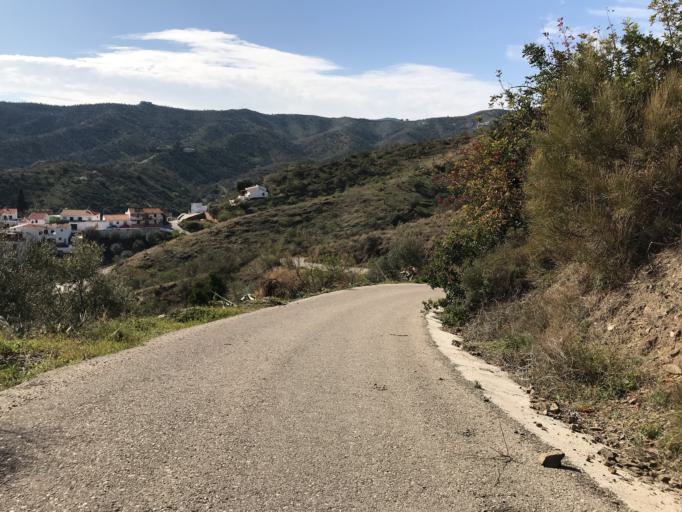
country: ES
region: Andalusia
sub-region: Provincia de Malaga
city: Valdes
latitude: 36.7717
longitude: -4.2144
